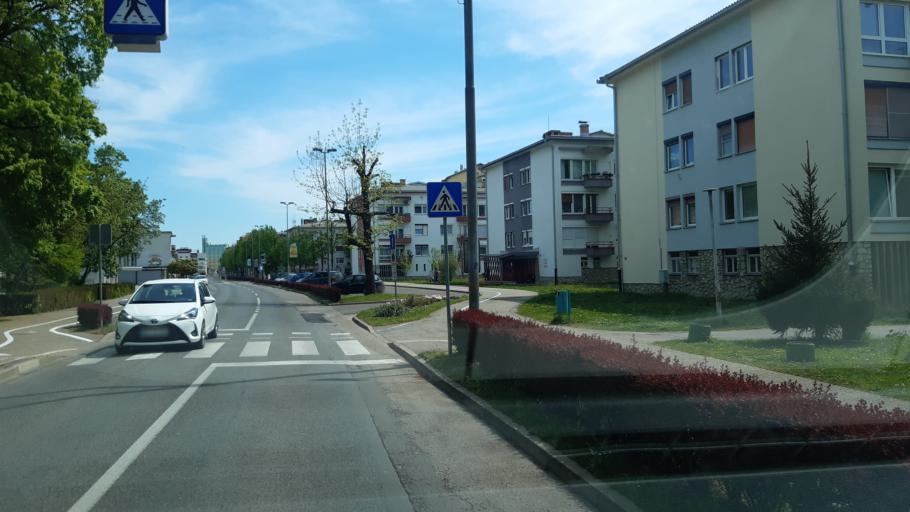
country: SI
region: Murska Sobota
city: Murska Sobota
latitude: 46.6607
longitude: 16.1584
